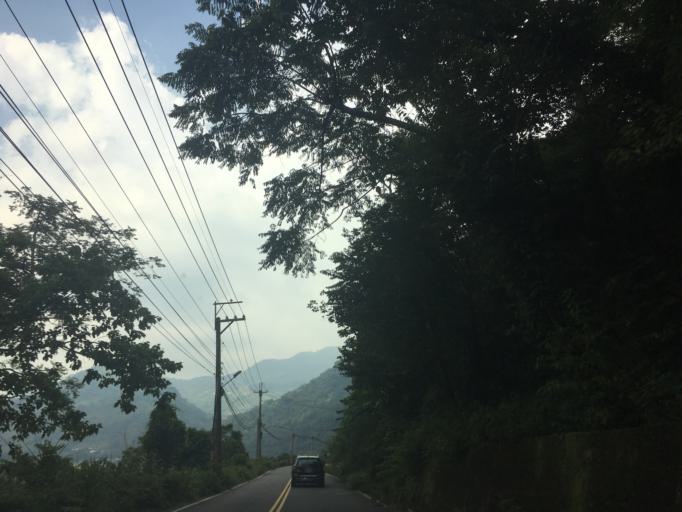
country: TW
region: Taiwan
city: Fengyuan
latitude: 24.2952
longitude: 120.9157
